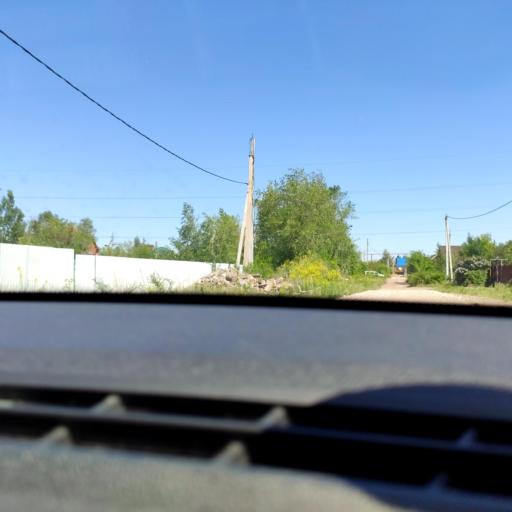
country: RU
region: Samara
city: Tol'yatti
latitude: 53.5596
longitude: 49.3810
